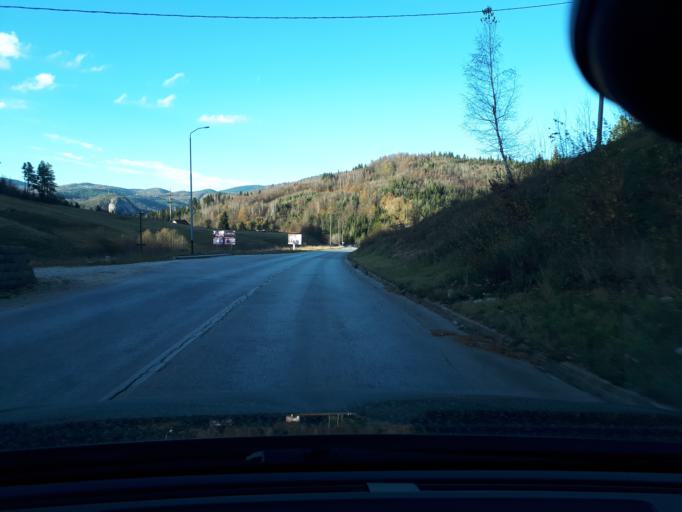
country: BA
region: Republika Srpska
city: Pale
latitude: 43.8321
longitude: 18.5579
